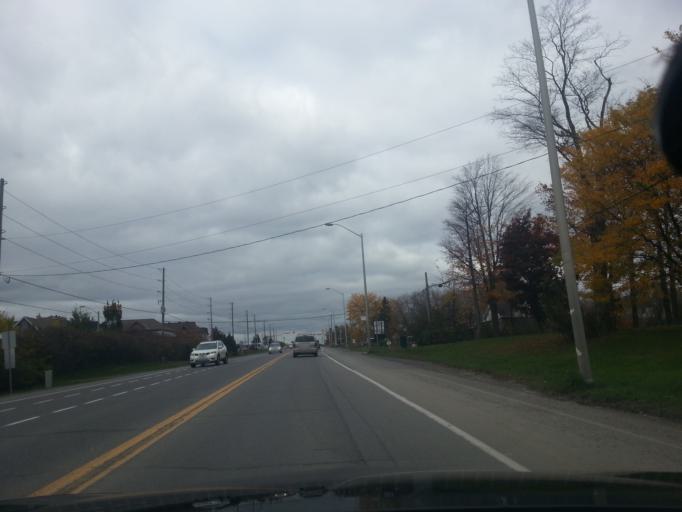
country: CA
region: Ontario
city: Ottawa
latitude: 45.3218
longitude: -75.5945
